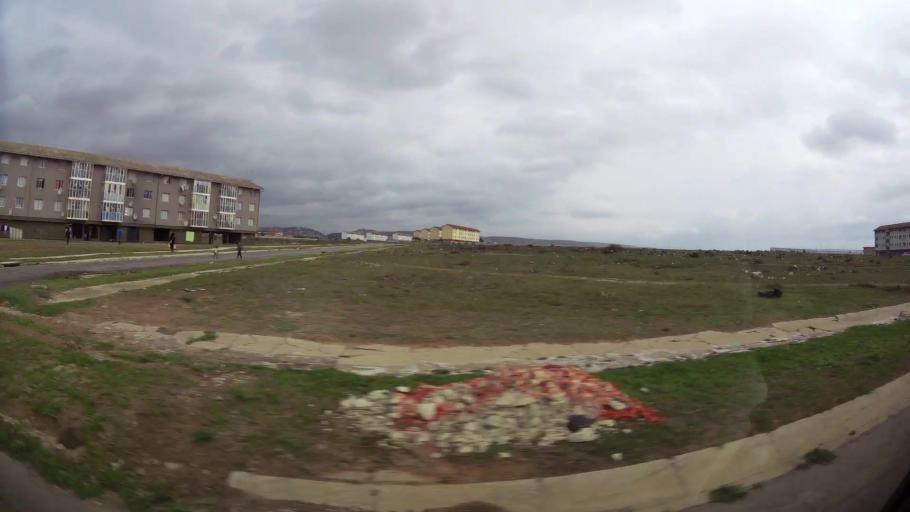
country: ZA
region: Eastern Cape
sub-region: Nelson Mandela Bay Metropolitan Municipality
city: Port Elizabeth
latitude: -33.8903
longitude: 25.5629
